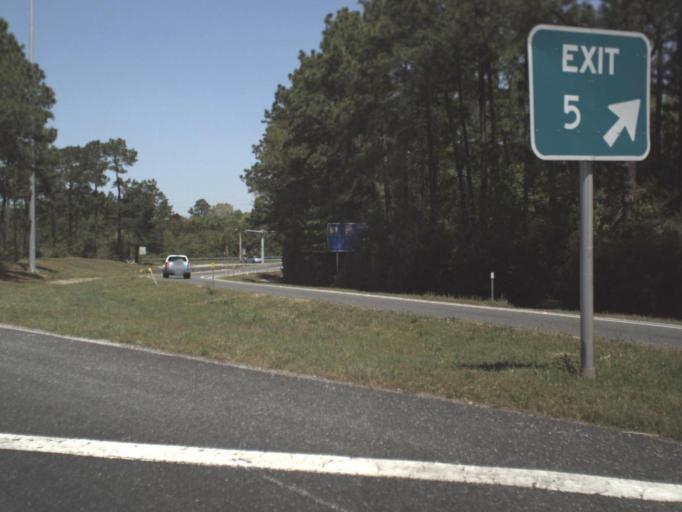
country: US
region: Florida
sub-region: Escambia County
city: Ensley
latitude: 30.5329
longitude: -87.3318
